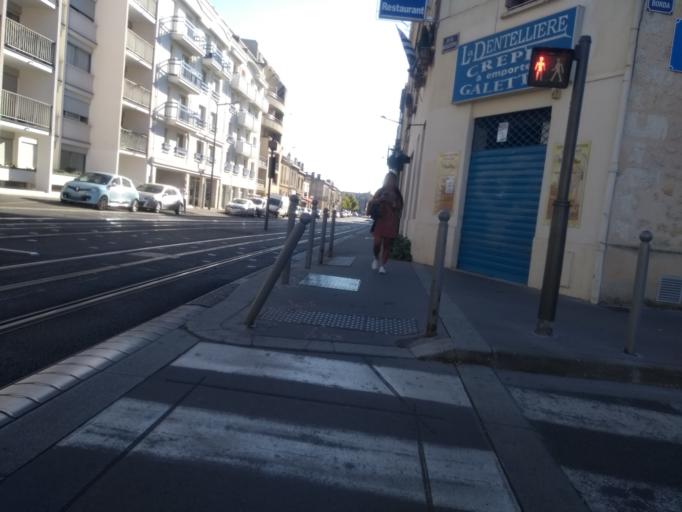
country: FR
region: Aquitaine
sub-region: Departement de la Gironde
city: Bordeaux
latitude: 44.8269
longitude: -0.5764
